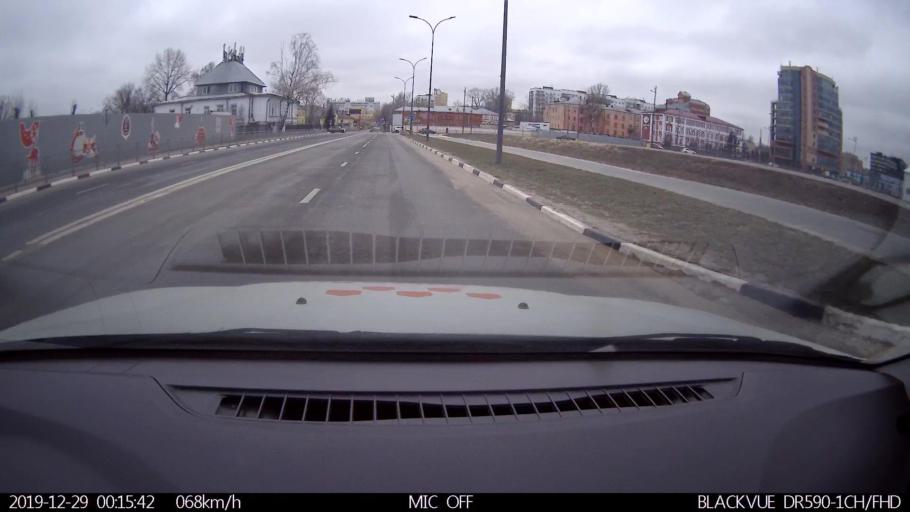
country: RU
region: Nizjnij Novgorod
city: Nizhniy Novgorod
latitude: 56.3328
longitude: 43.9673
